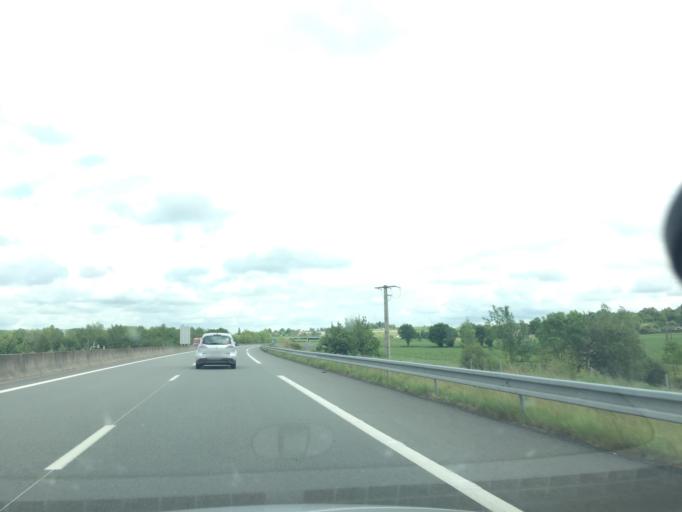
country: FR
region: Pays de la Loire
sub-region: Departement de la Sarthe
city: Chateau-du-Loir
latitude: 47.6617
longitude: 0.4237
